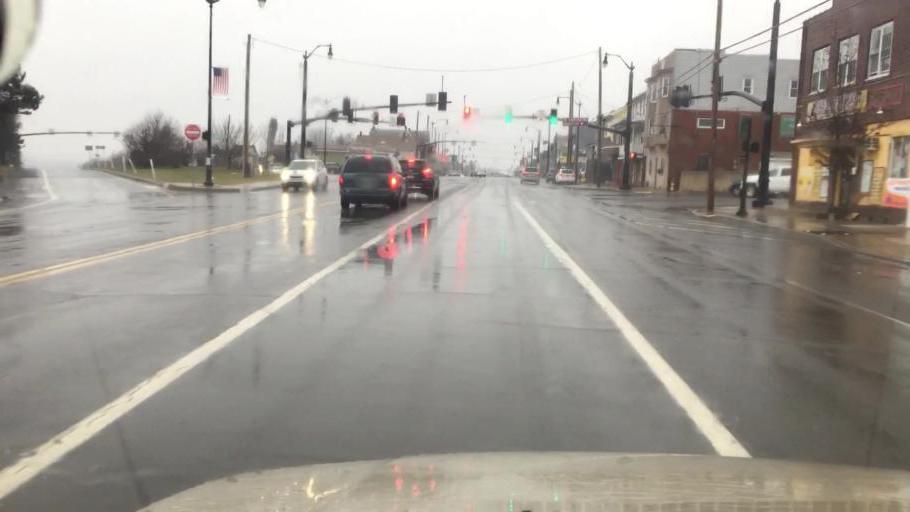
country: US
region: Pennsylvania
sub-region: Luzerne County
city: West Hazleton
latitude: 40.9574
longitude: -75.9876
